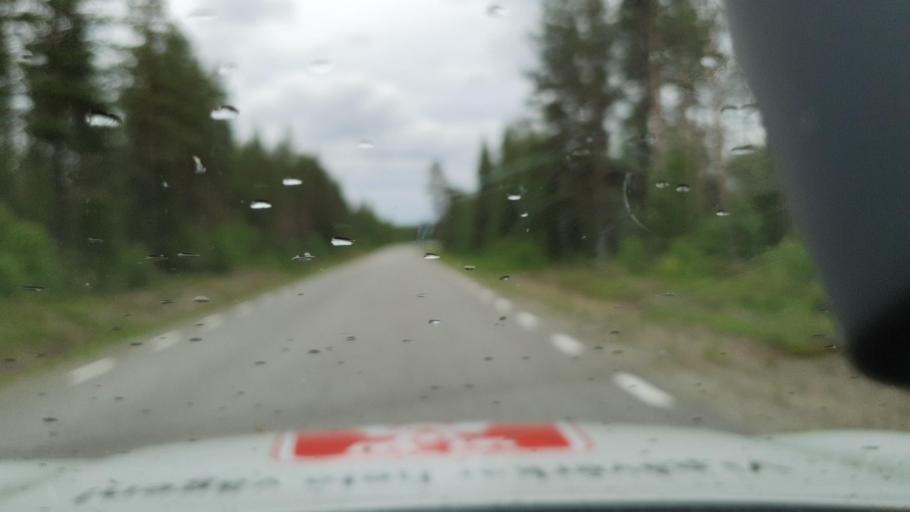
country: SE
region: Vaesterbotten
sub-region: Lycksele Kommun
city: Lycksele
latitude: 64.2294
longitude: 18.2432
